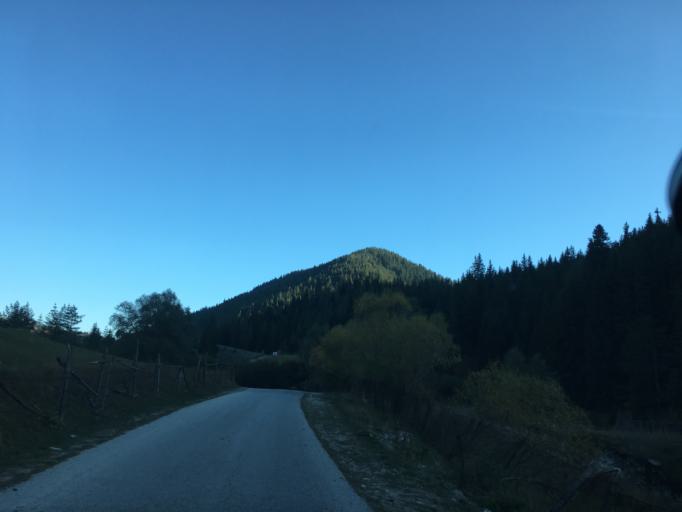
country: BG
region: Smolyan
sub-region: Obshtina Borino
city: Borino
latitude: 41.5863
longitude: 24.3886
